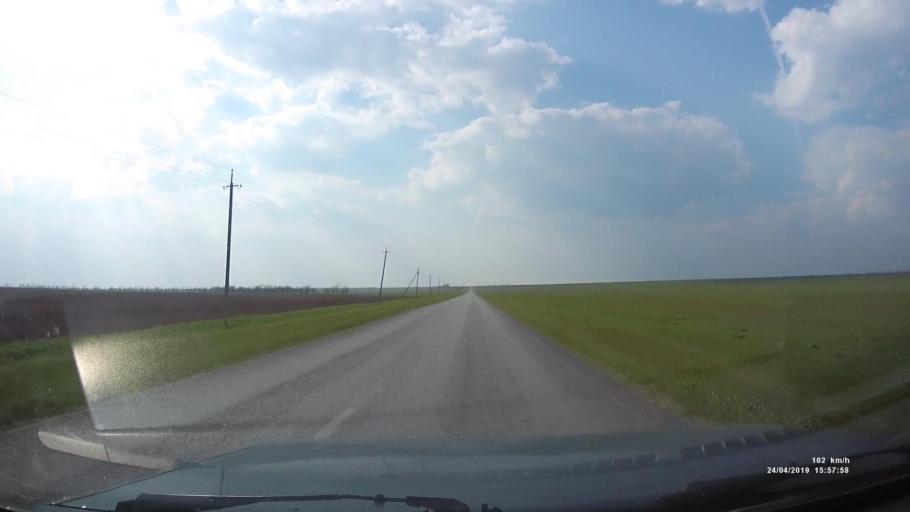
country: RU
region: Kalmykiya
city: Yashalta
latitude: 46.6098
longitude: 42.4988
